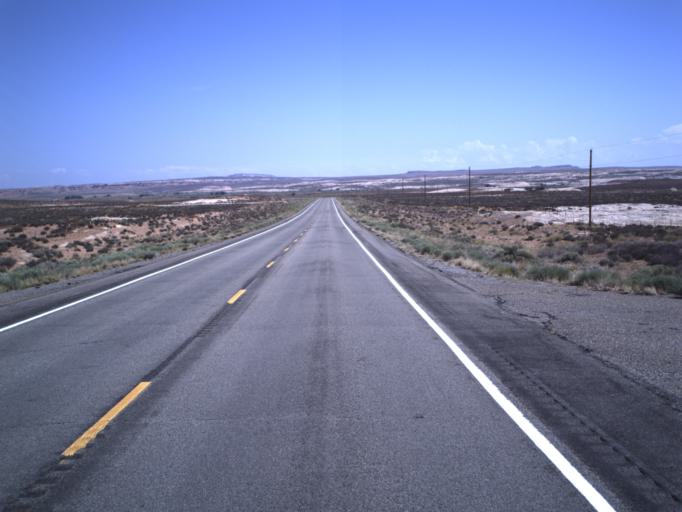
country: US
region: Utah
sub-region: San Juan County
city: Blanding
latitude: 37.0647
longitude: -109.5581
